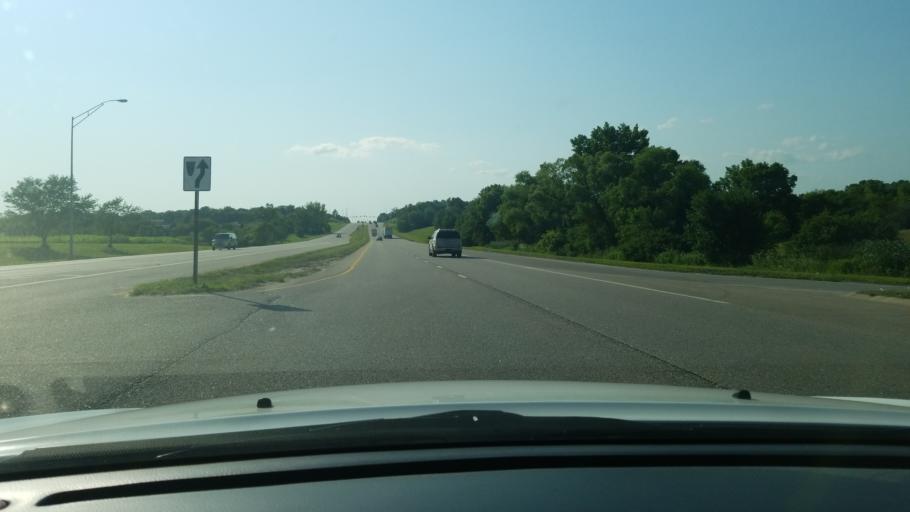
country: US
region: Nebraska
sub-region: Lancaster County
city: Lincoln
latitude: 40.7422
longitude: -96.6179
